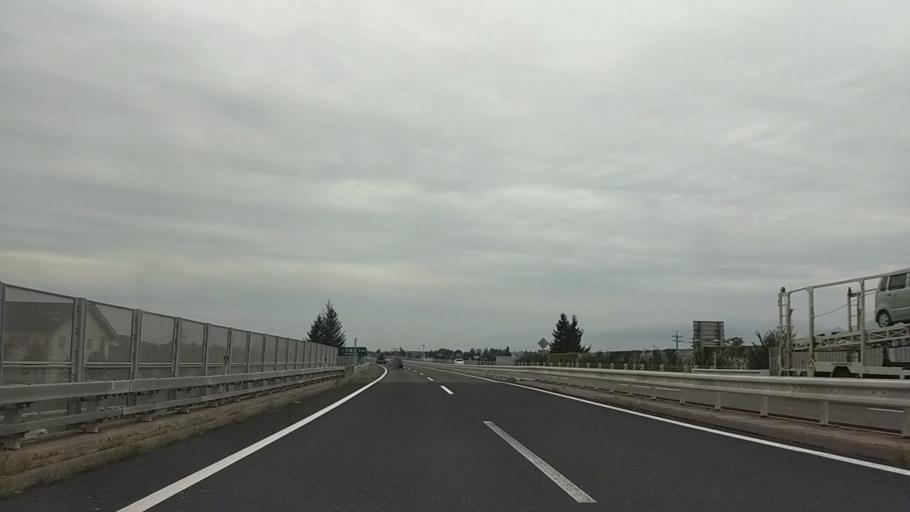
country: JP
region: Nagano
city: Toyoshina
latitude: 36.3171
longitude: 137.9206
